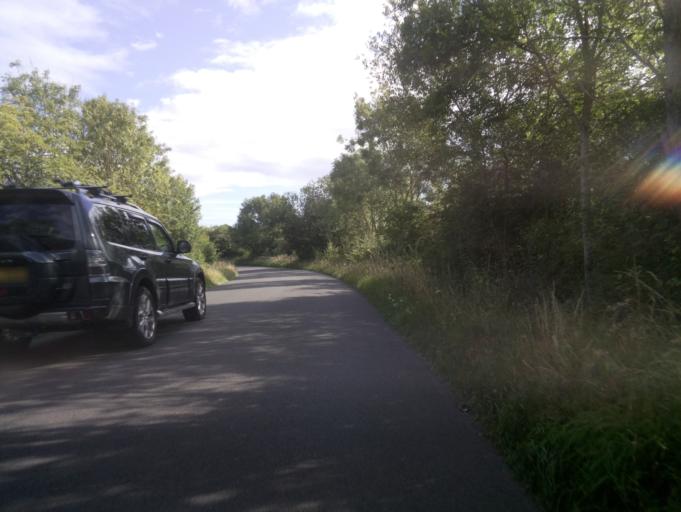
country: GB
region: England
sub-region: Gloucestershire
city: Gloucester
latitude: 51.8110
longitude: -2.2642
